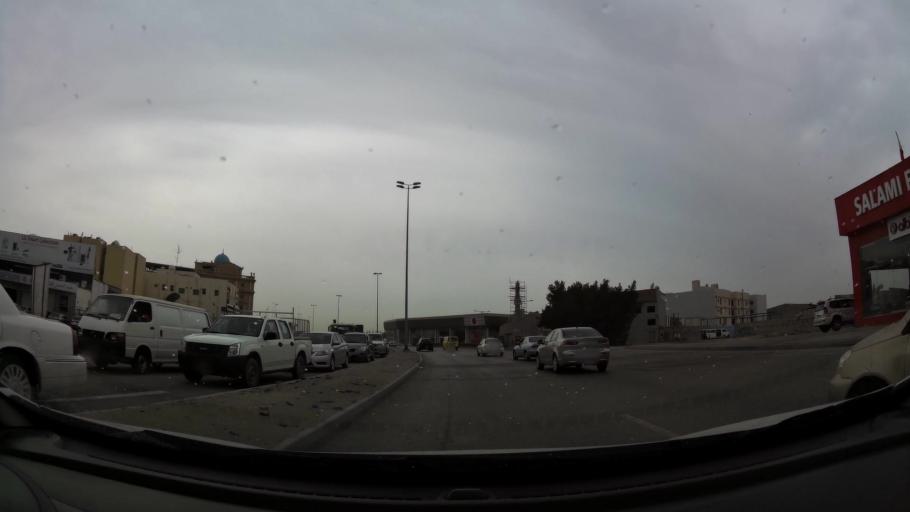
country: BH
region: Manama
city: Jidd Hafs
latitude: 26.2027
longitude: 50.5338
